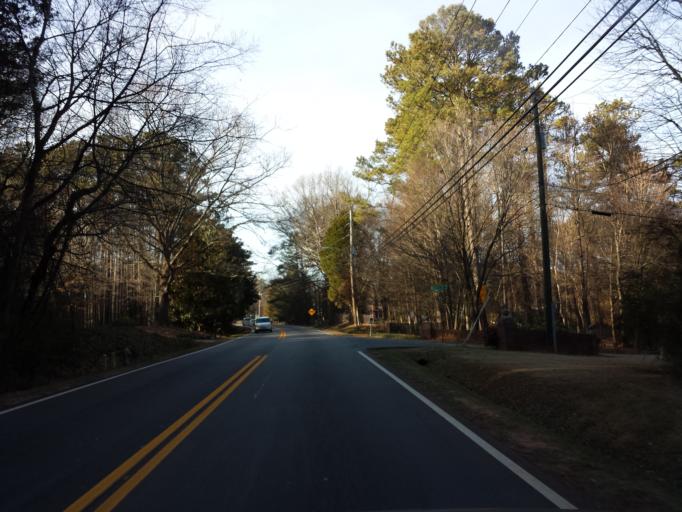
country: US
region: Georgia
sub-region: Cobb County
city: Kennesaw
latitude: 34.0428
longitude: -84.5522
